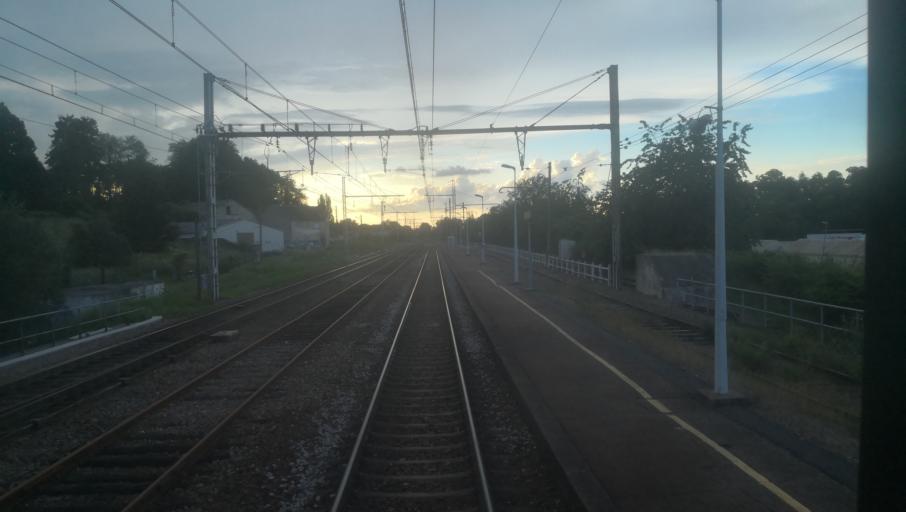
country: FR
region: Limousin
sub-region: Departement de la Creuse
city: La Souterraine
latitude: 46.2421
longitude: 1.4904
